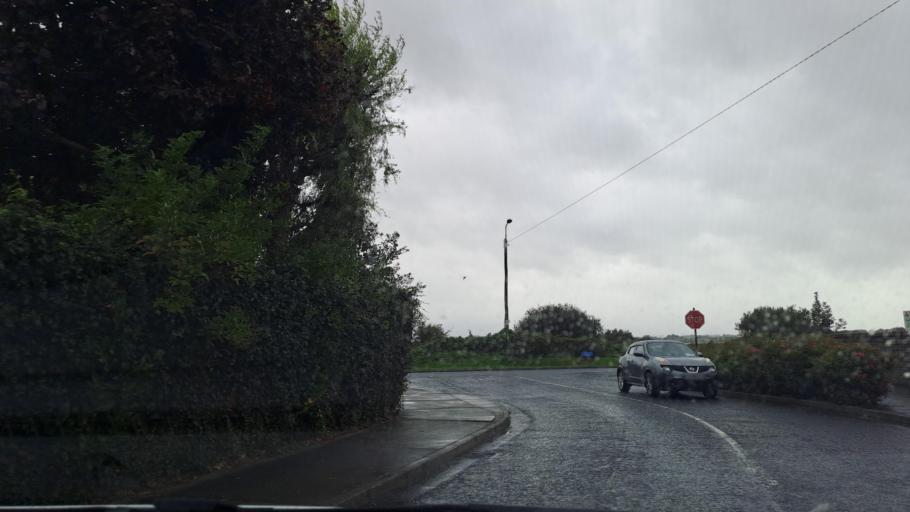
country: IE
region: Leinster
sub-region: Lu
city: Blackrock
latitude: 53.9576
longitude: -6.3754
